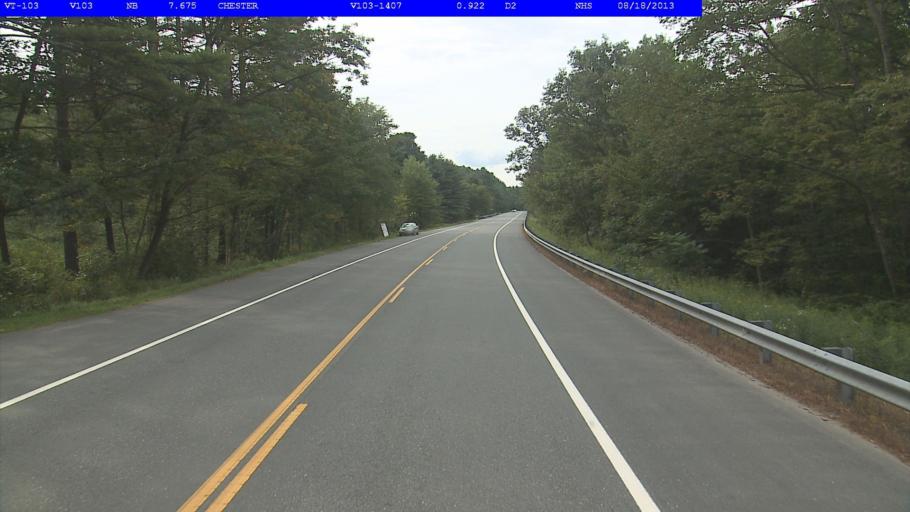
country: US
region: Vermont
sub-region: Windsor County
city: Chester
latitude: 43.2432
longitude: -72.5676
